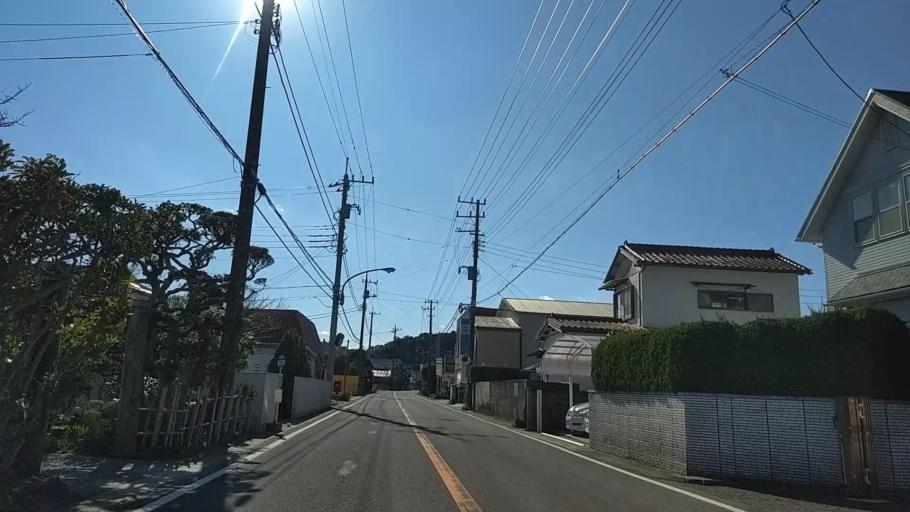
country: JP
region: Chiba
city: Tateyama
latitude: 34.9784
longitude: 139.8633
